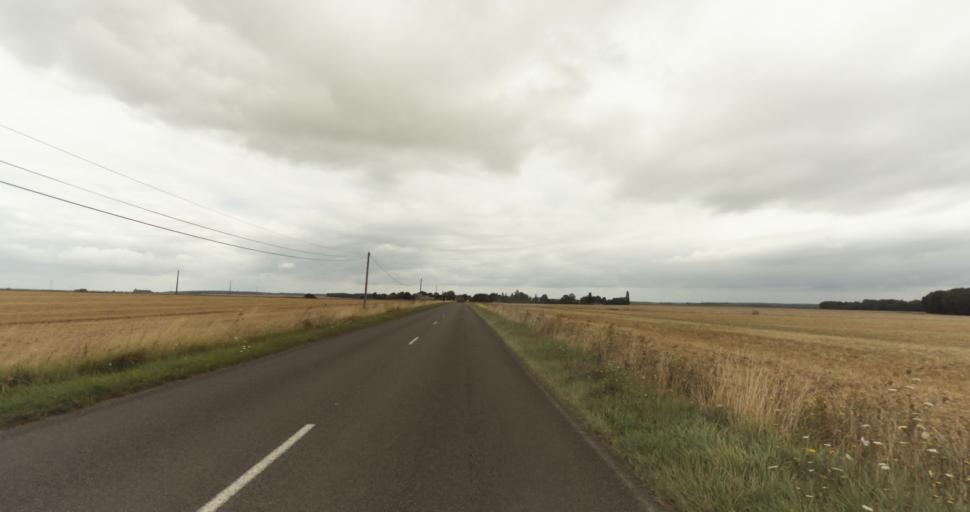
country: FR
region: Haute-Normandie
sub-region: Departement de l'Eure
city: Gravigny
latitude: 49.0473
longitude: 1.2176
